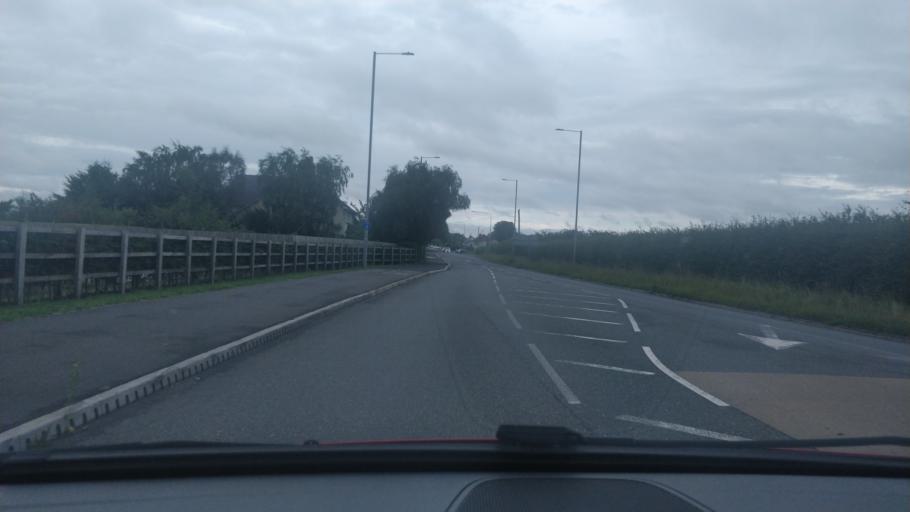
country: GB
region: England
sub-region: Cheshire West and Chester
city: Saughall
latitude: 53.1721
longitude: -2.9680
